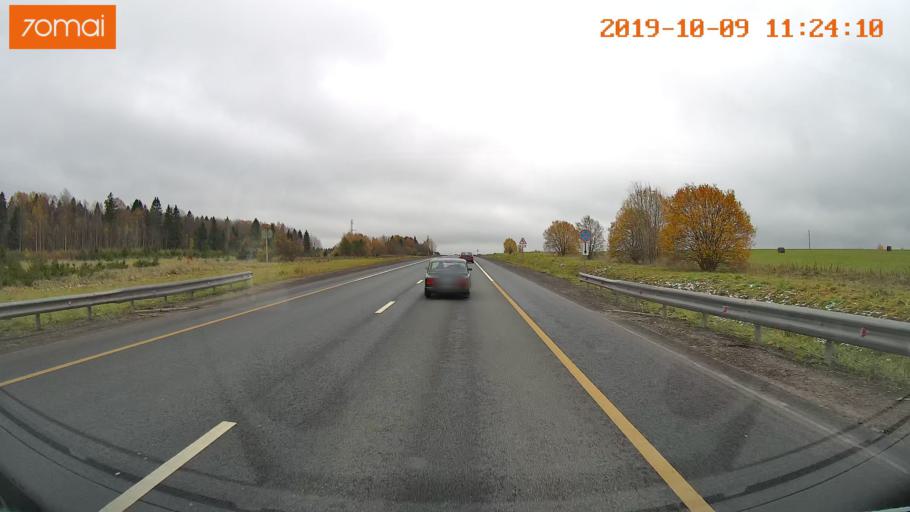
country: RU
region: Vologda
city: Vologda
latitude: 59.1141
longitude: 39.9772
